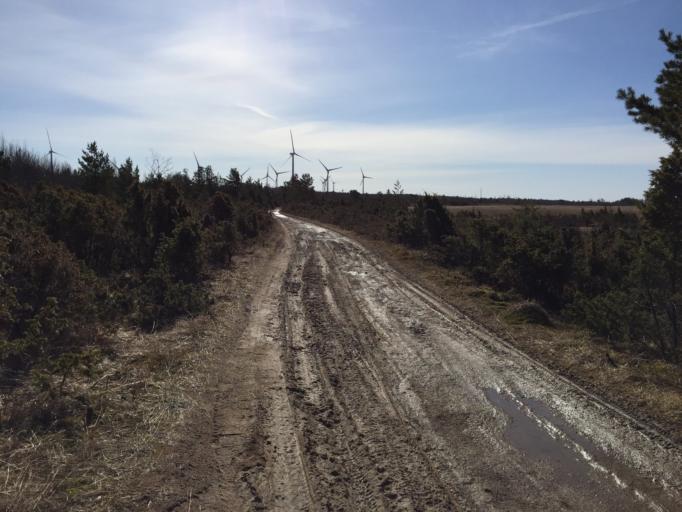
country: EE
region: Laeaene
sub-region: Haapsalu linn
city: Haapsalu
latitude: 58.6490
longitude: 23.5091
